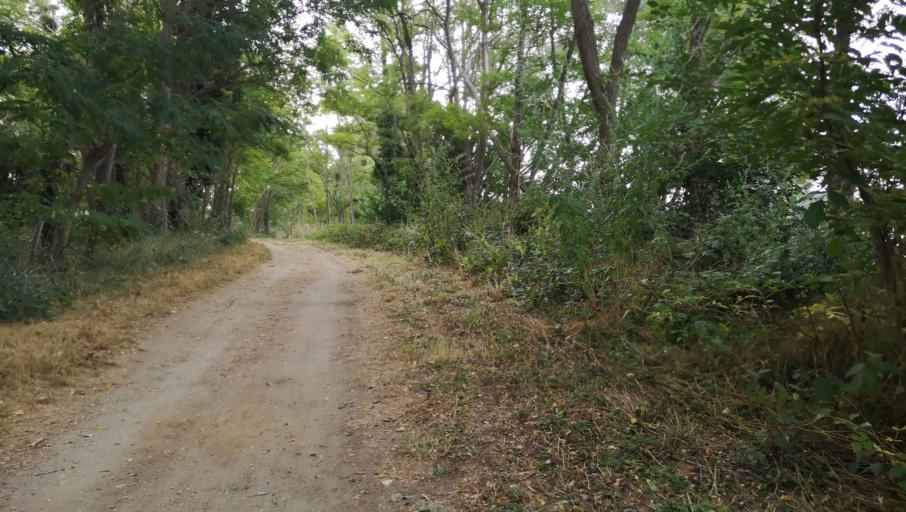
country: FR
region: Centre
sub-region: Departement du Loiret
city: Checy
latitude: 47.8891
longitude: 2.0106
